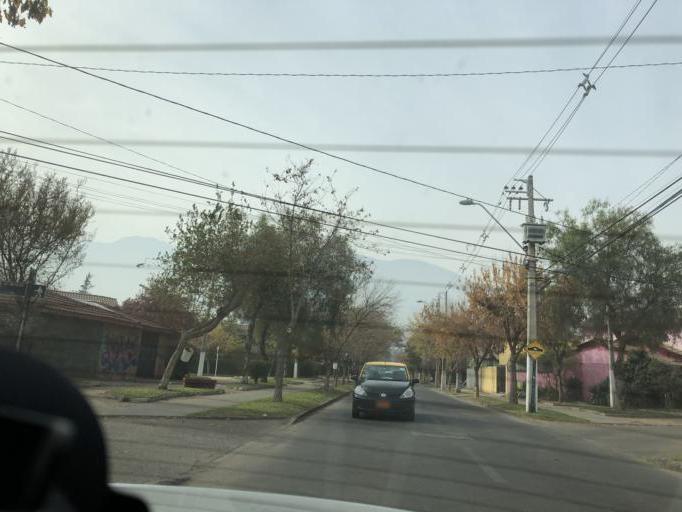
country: CL
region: Santiago Metropolitan
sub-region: Provincia de Cordillera
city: Puente Alto
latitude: -33.5492
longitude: -70.5625
